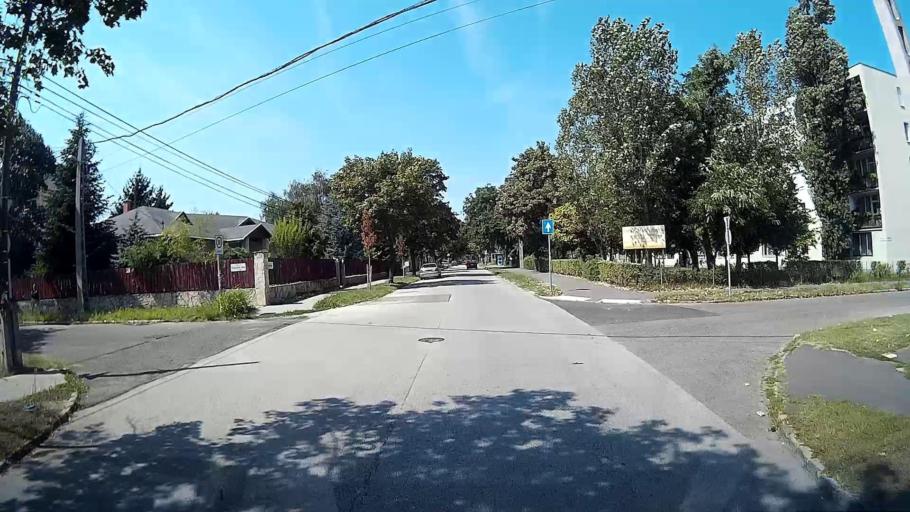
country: HU
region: Budapest
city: Budapest X. keruelet
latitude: 47.4831
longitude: 19.1498
